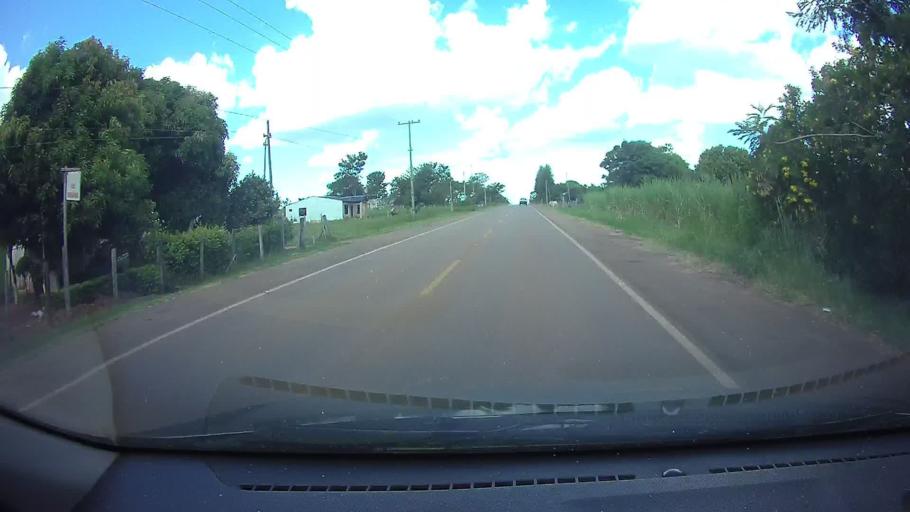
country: PY
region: Paraguari
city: La Colmena
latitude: -25.9180
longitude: -56.7308
